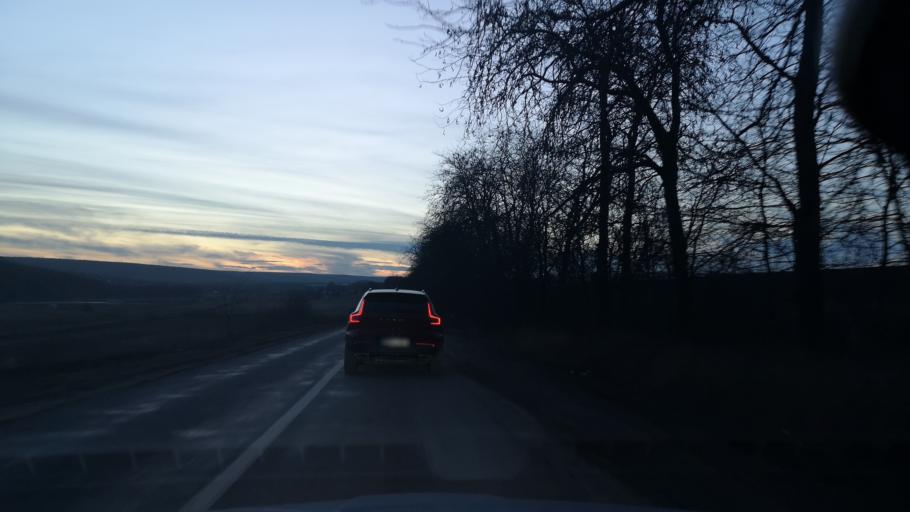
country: MD
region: Orhei
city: Orhei
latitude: 47.2986
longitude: 28.9101
